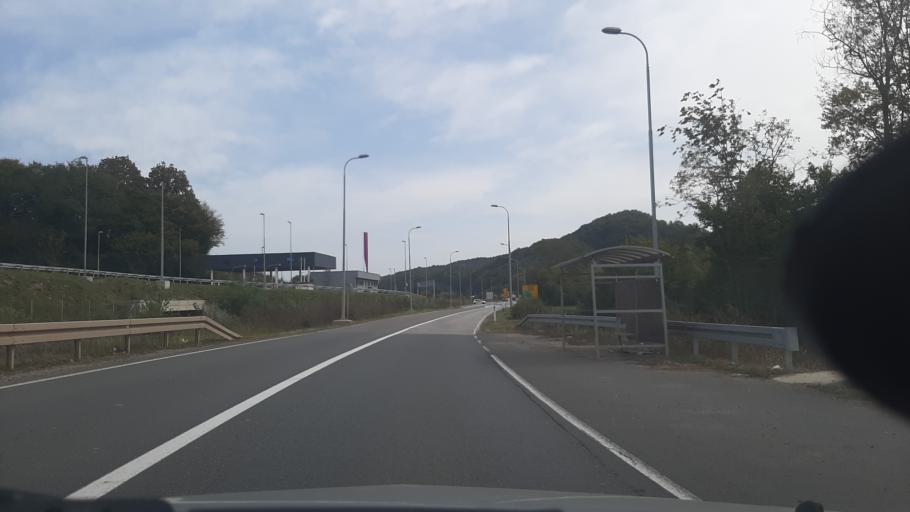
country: BA
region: Republika Srpska
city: Maglajani
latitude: 44.8705
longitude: 17.4024
